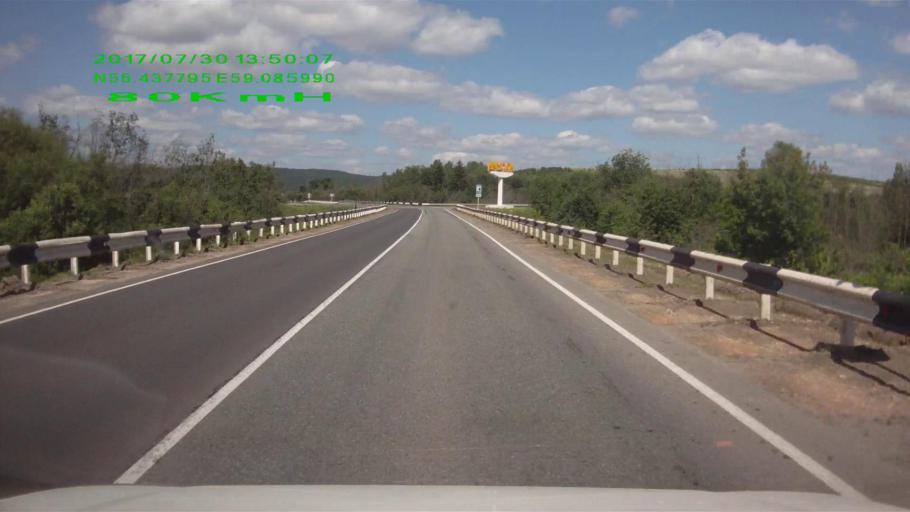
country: RU
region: Sverdlovsk
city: Mikhaylovsk
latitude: 56.4383
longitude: 59.0862
